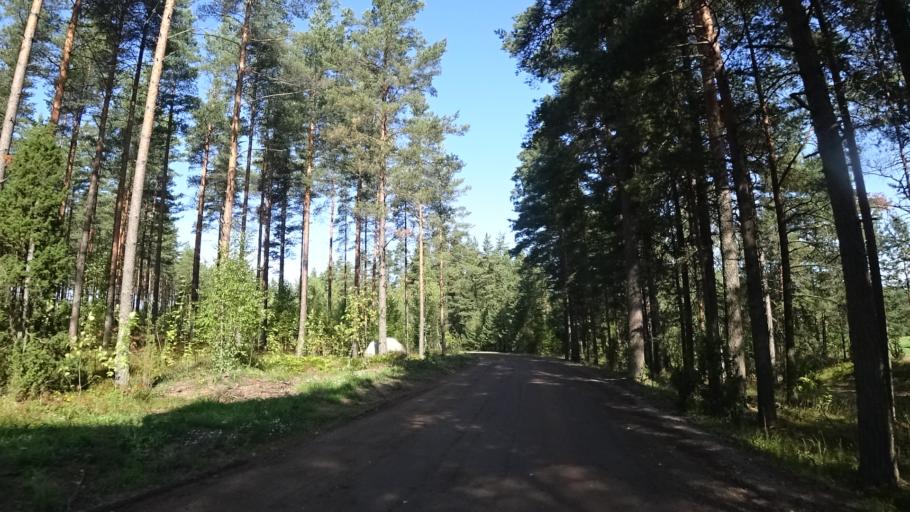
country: FI
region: Kymenlaakso
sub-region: Kotka-Hamina
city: Hamina
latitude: 60.5450
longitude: 27.2180
